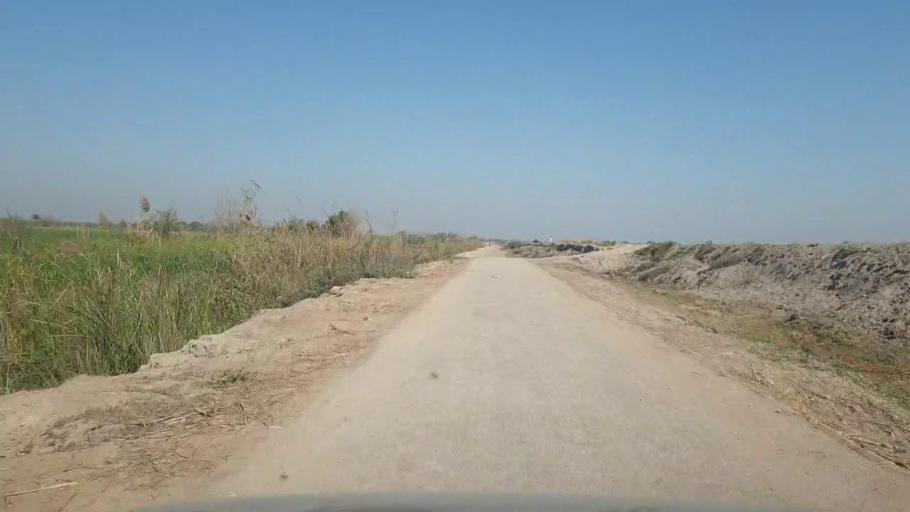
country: PK
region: Sindh
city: Mirwah Gorchani
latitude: 25.3344
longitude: 69.1019
